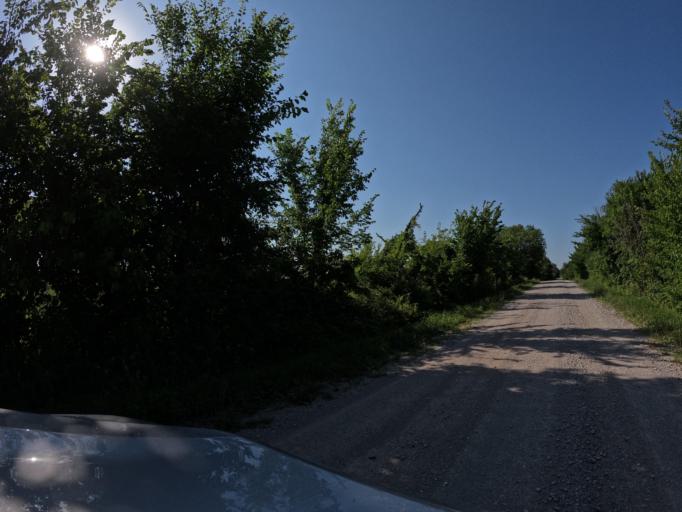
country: US
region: Iowa
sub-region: Appanoose County
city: Centerville
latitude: 40.7354
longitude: -93.0206
